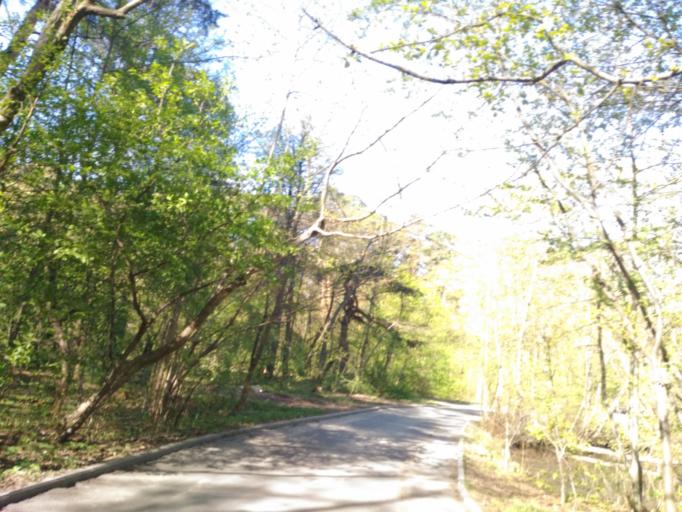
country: RU
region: Moscow
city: Shchukino
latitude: 55.7814
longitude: 37.4227
